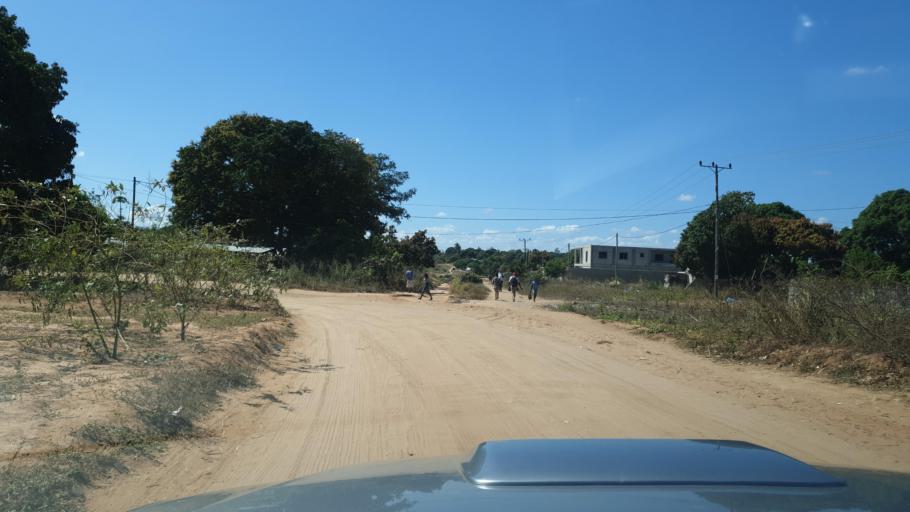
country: MZ
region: Nampula
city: Nampula
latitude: -15.1020
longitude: 39.2065
